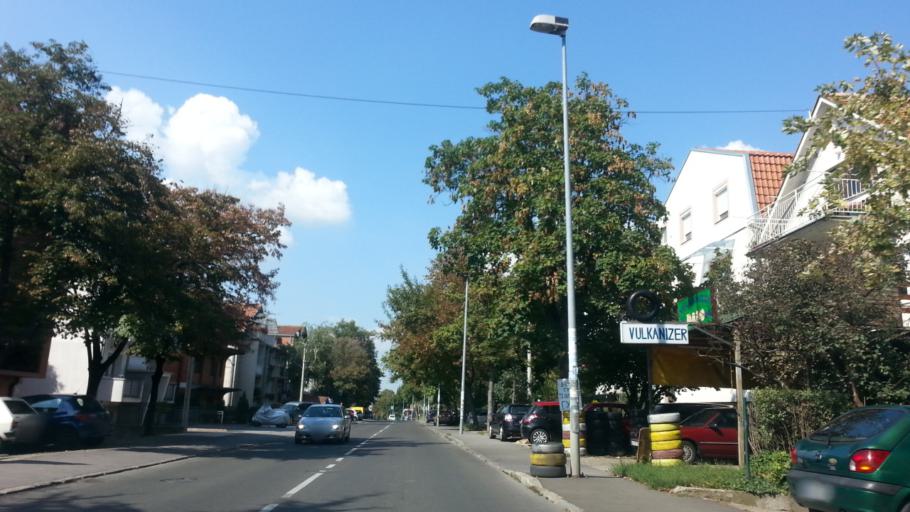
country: RS
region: Central Serbia
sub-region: Belgrade
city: Cukarica
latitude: 44.7669
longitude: 20.4226
